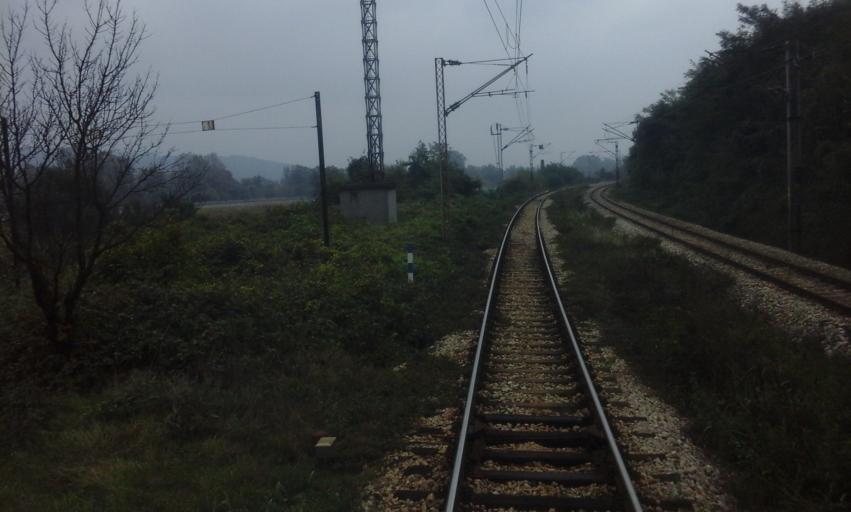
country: RS
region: Central Serbia
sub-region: Pomoravski Okrug
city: Jagodina
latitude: 44.0798
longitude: 21.1860
